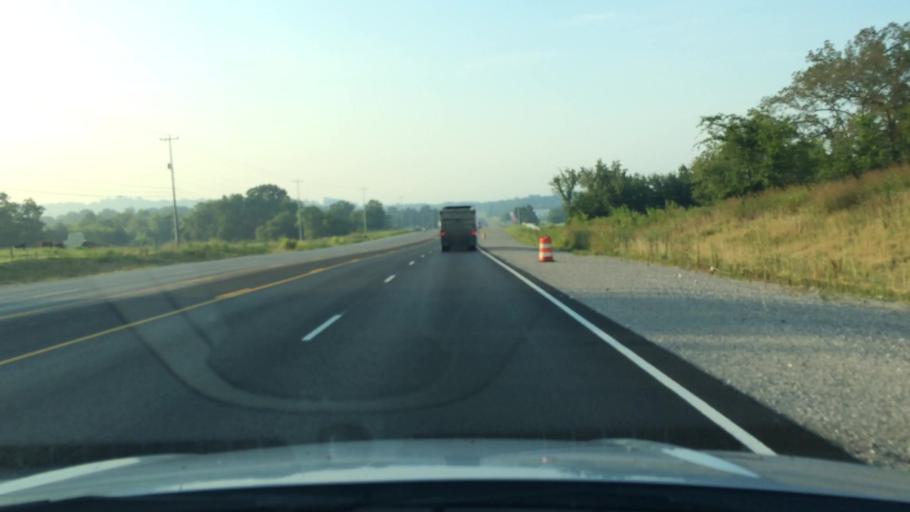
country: US
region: Tennessee
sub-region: Giles County
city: Pulaski
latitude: 35.1628
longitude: -87.0109
